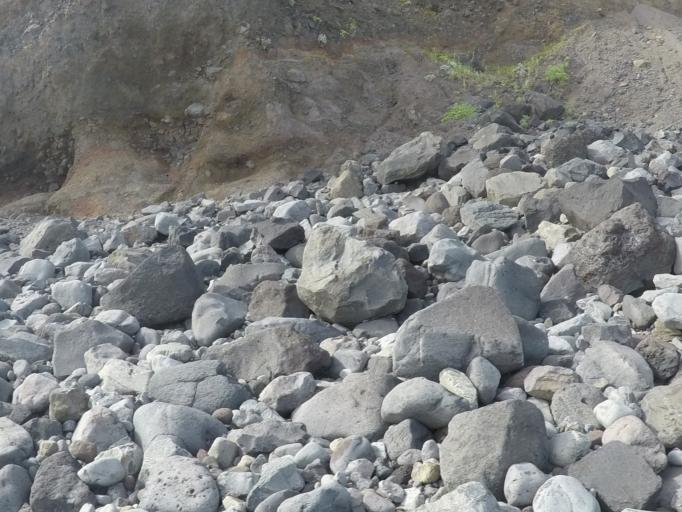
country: PT
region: Madeira
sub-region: Sao Vicente
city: Sao Vicente
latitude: 32.8094
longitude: -16.9690
